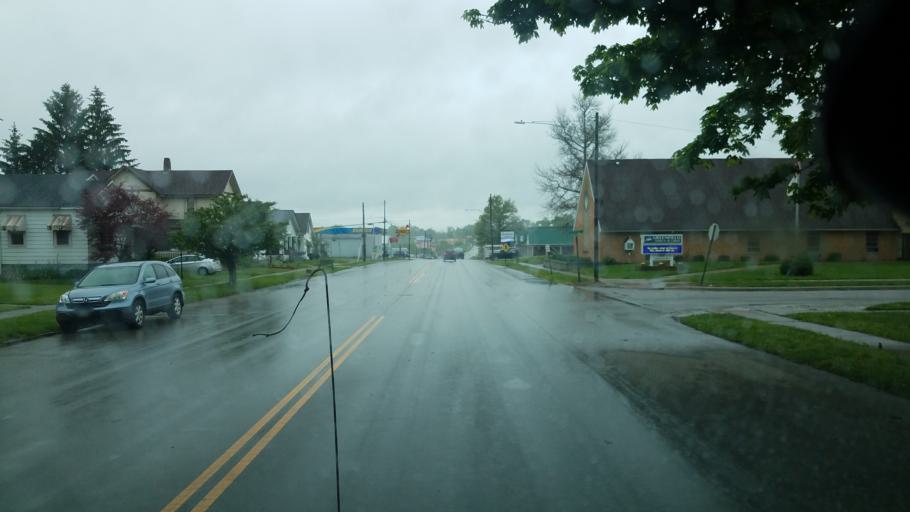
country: US
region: Ohio
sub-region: Highland County
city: Greenfield
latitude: 39.3489
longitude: -83.3953
